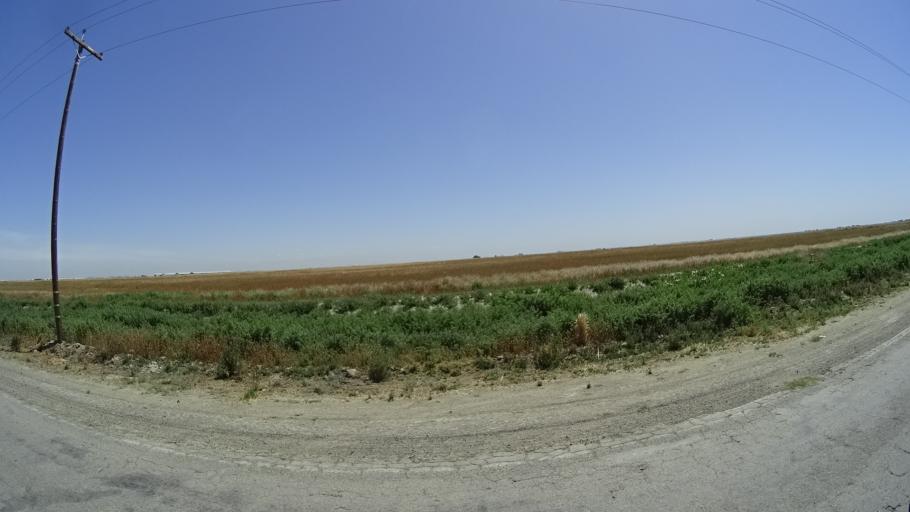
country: US
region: California
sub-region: Kings County
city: Stratford
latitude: 36.1537
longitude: -119.7173
